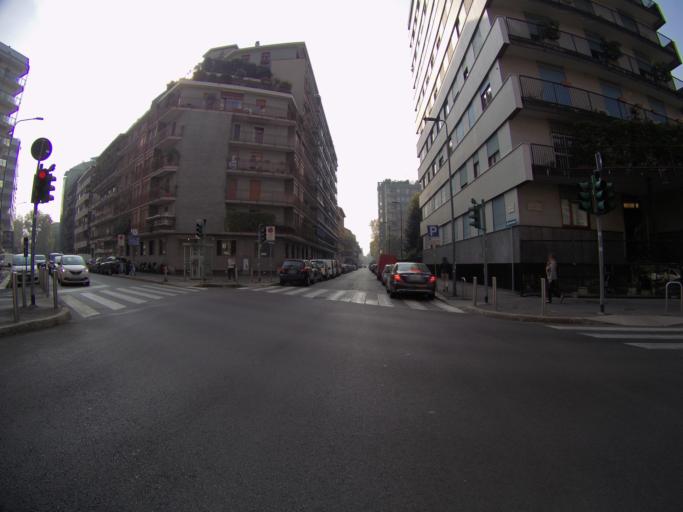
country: IT
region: Lombardy
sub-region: Citta metropolitana di Milano
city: Milano
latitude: 45.4759
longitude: 9.2194
